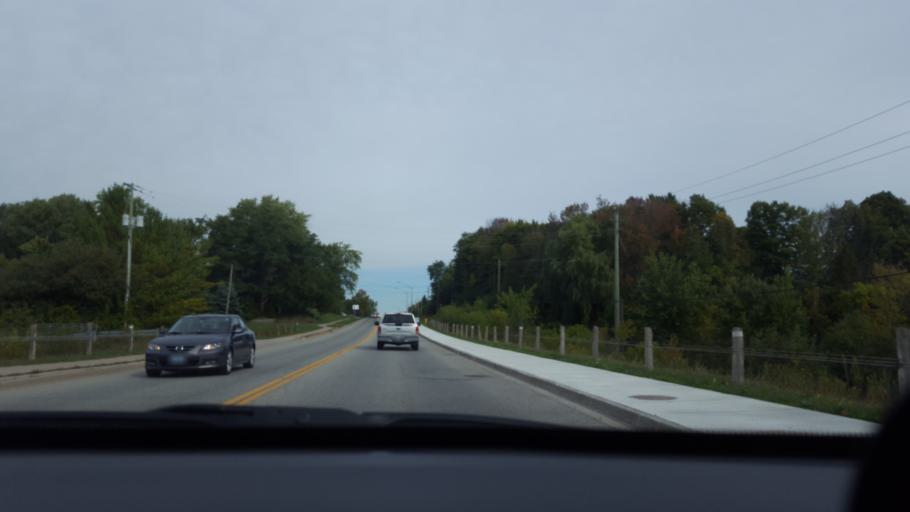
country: CA
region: Ontario
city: Vaughan
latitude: 43.9352
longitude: -79.5299
